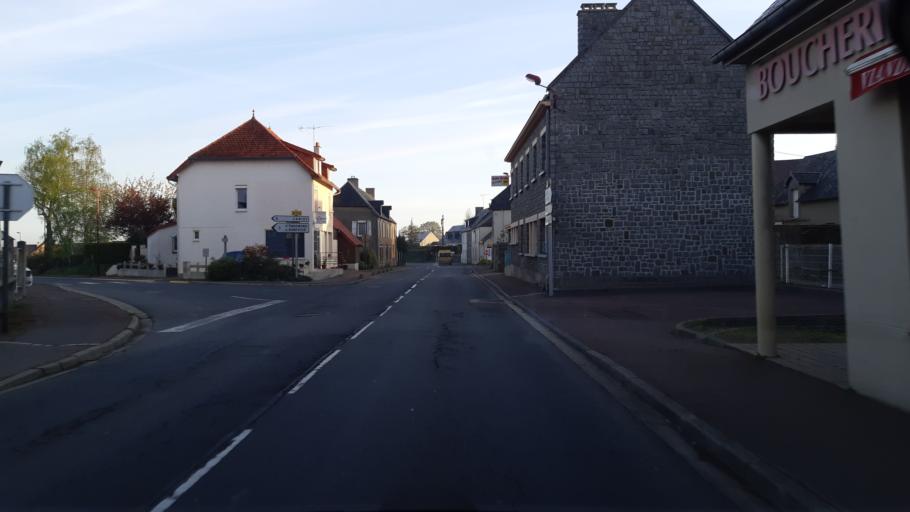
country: FR
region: Lower Normandy
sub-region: Departement de la Manche
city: Agneaux
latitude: 49.0494
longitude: -1.1286
